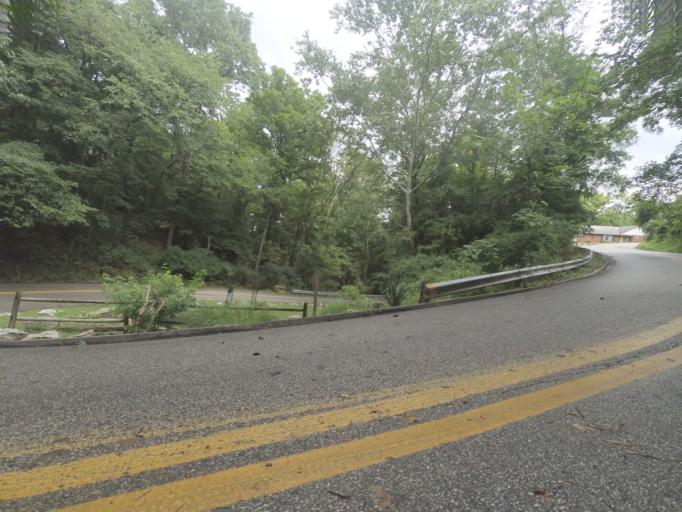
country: US
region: West Virginia
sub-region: Cabell County
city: Huntington
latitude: 38.4005
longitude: -82.4501
